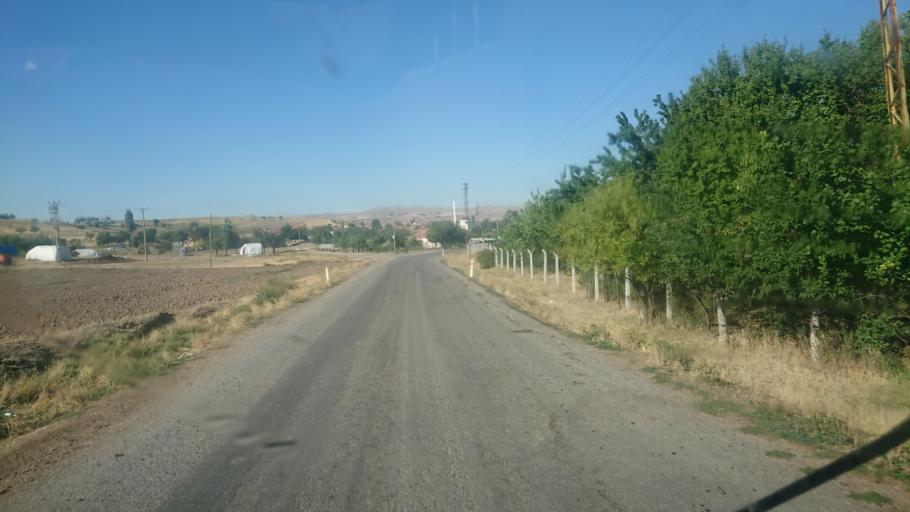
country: TR
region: Aksaray
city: Agacoren
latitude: 38.8183
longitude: 33.7239
